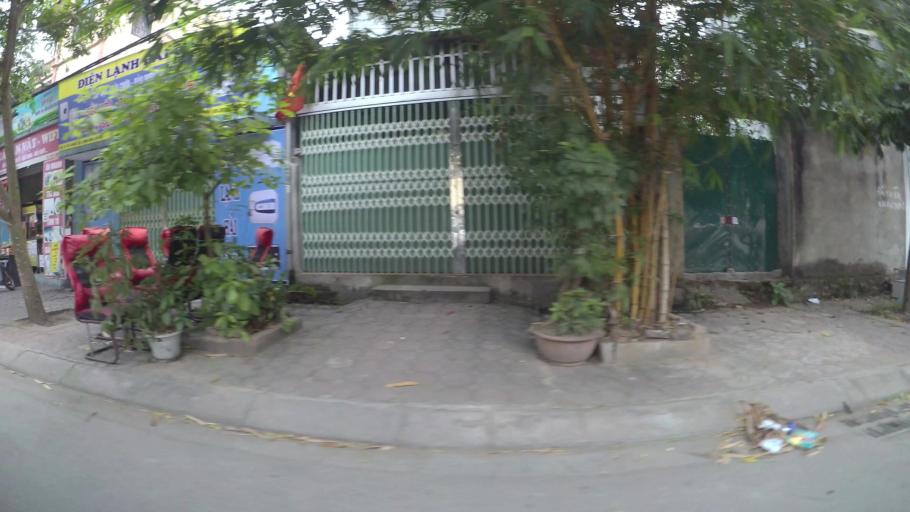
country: VN
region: Ha Noi
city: Trau Quy
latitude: 21.0448
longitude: 105.9256
